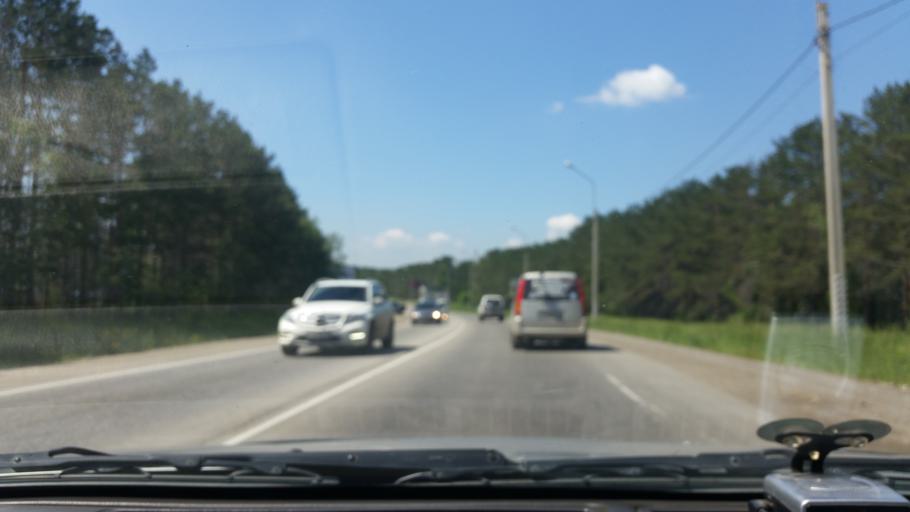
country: RU
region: Irkutsk
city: Smolenshchina
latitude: 52.2603
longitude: 104.1862
